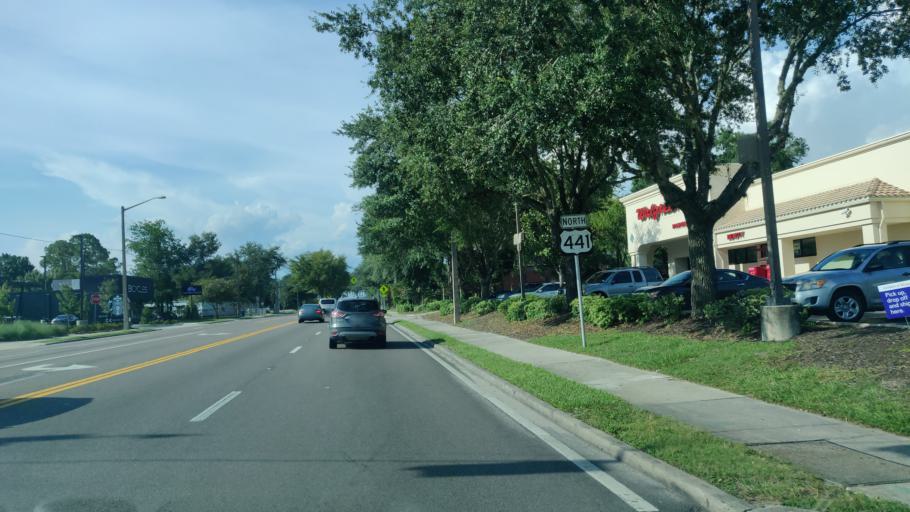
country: US
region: Florida
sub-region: Alachua County
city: Gainesville
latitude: 29.6667
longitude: -82.3391
